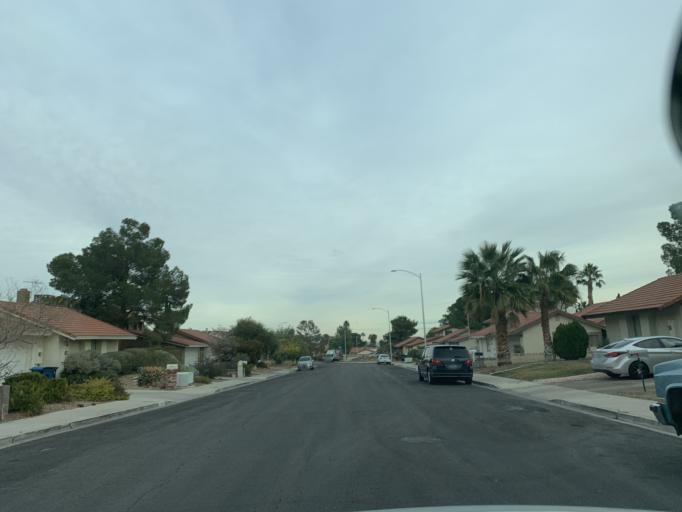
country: US
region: Nevada
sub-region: Clark County
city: Summerlin South
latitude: 36.1561
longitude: -115.2901
